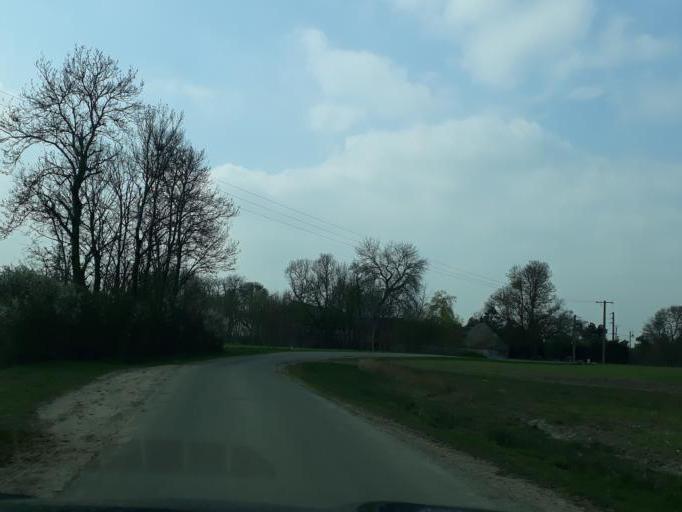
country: FR
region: Centre
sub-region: Departement d'Eure-et-Loir
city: Baigneaux
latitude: 48.0991
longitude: 1.8245
